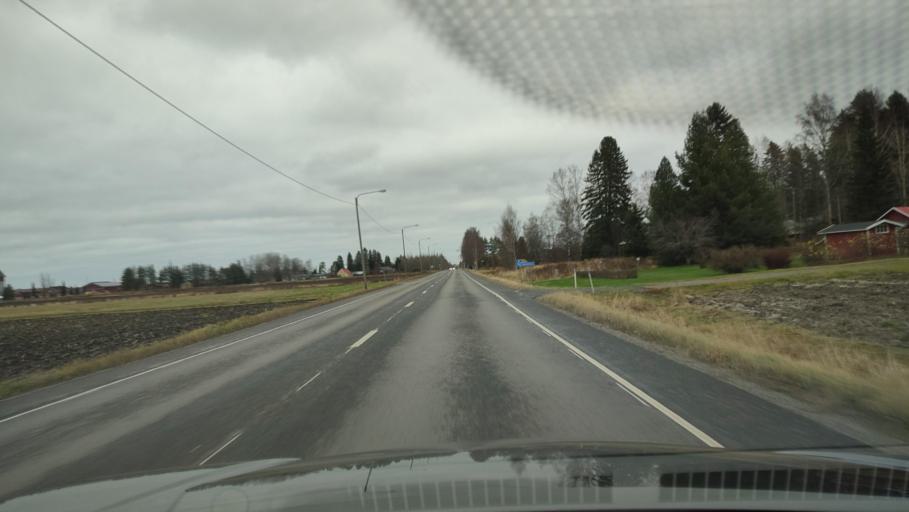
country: FI
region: Southern Ostrobothnia
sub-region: Seinaejoki
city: Ilmajoki
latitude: 62.6917
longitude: 22.4957
